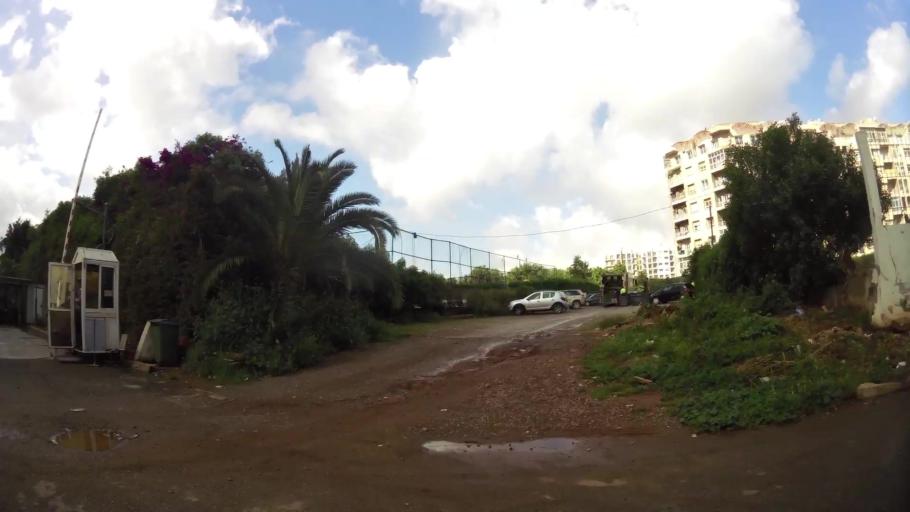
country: MA
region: Grand Casablanca
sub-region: Casablanca
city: Casablanca
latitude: 33.5534
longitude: -7.6279
